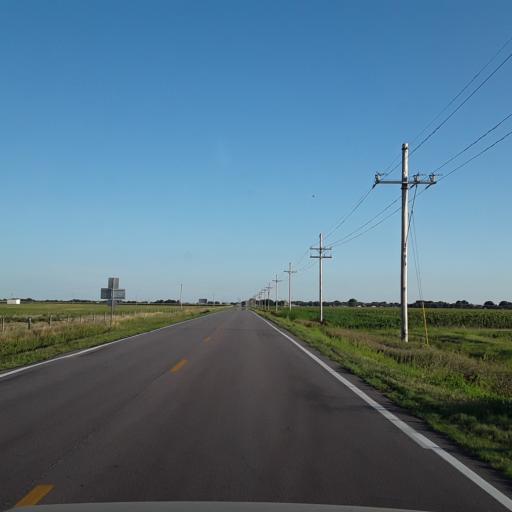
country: US
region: Nebraska
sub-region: Hall County
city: Grand Island
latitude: 40.9598
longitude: -98.3207
